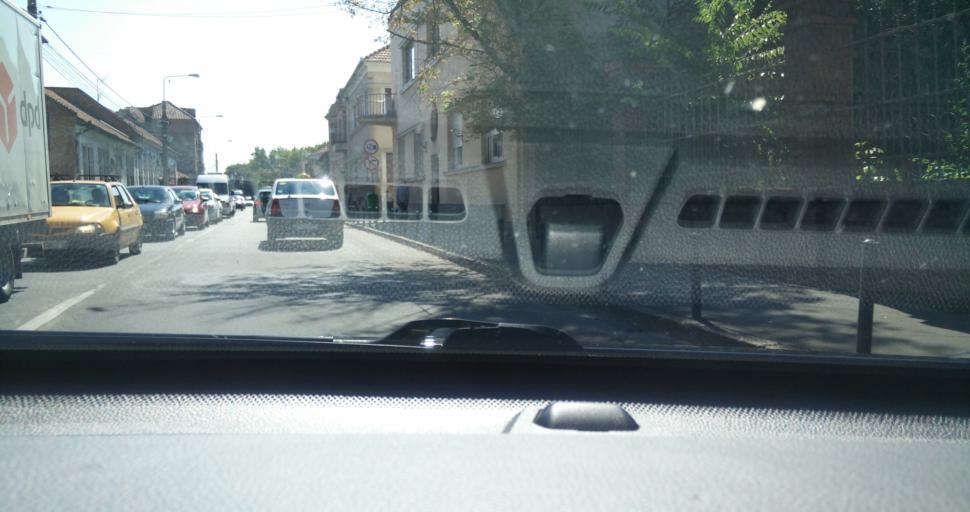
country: RO
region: Bihor
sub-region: Comuna Biharea
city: Oradea
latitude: 47.0503
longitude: 21.9263
